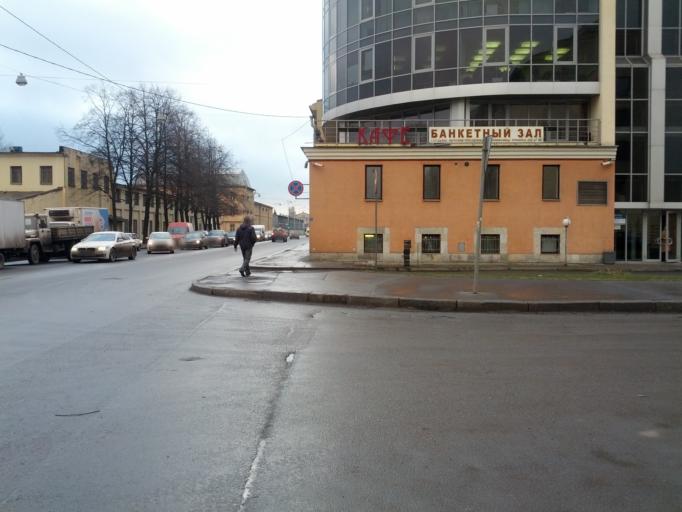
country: RU
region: St.-Petersburg
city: Centralniy
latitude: 59.9123
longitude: 30.3586
